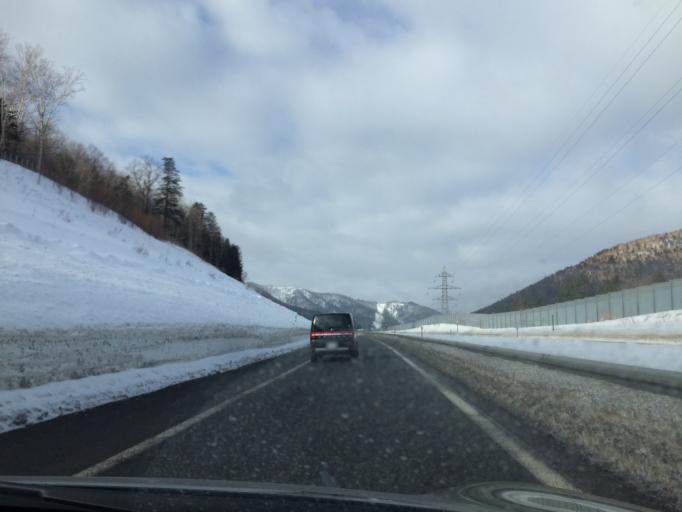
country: JP
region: Hokkaido
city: Shimo-furano
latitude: 43.0543
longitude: 142.6047
